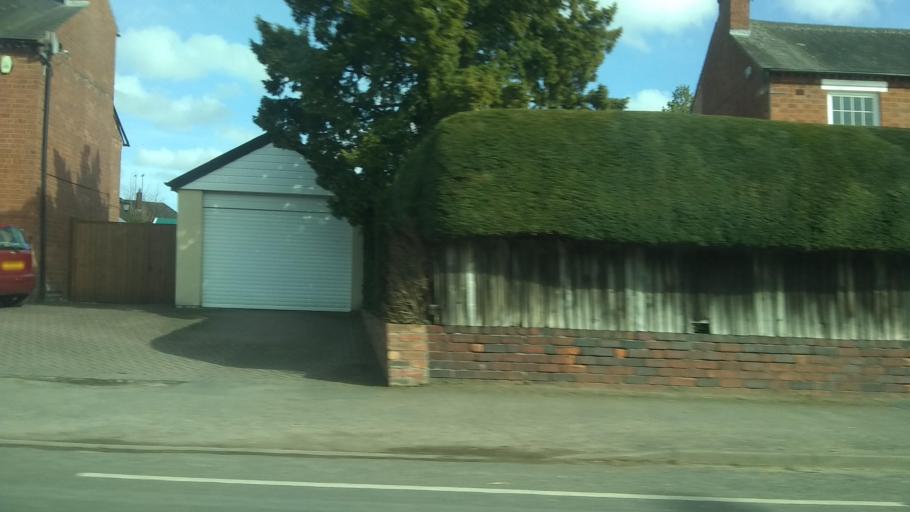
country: GB
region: England
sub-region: Worcestershire
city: Stourport-on-Severn
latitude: 52.3475
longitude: -2.2831
